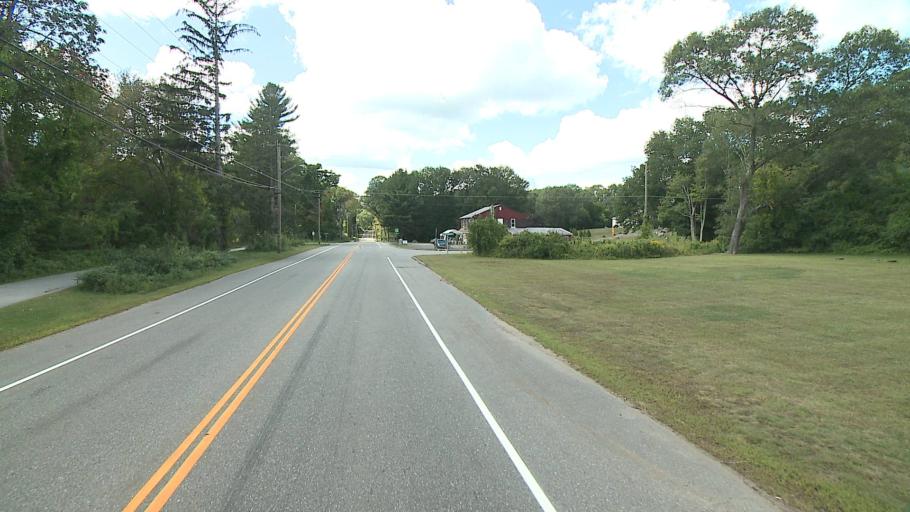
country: US
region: Connecticut
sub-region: Tolland County
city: Storrs
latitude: 41.8230
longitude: -72.2777
